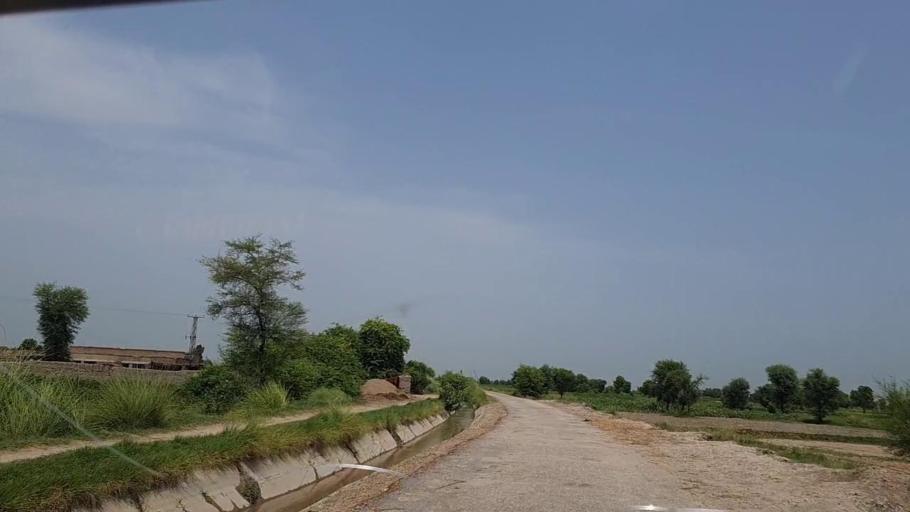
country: PK
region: Sindh
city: Tharu Shah
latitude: 26.9275
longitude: 68.0682
